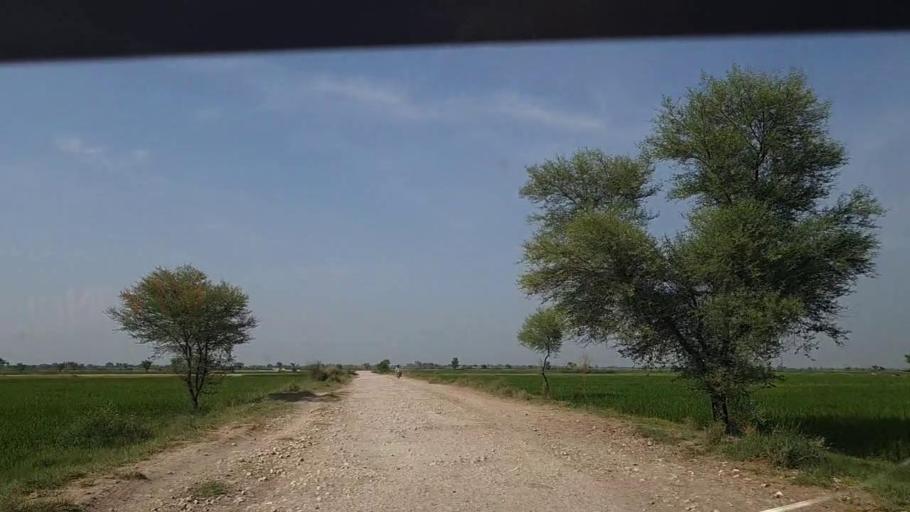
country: PK
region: Sindh
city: Khanpur
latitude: 27.8465
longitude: 69.3772
